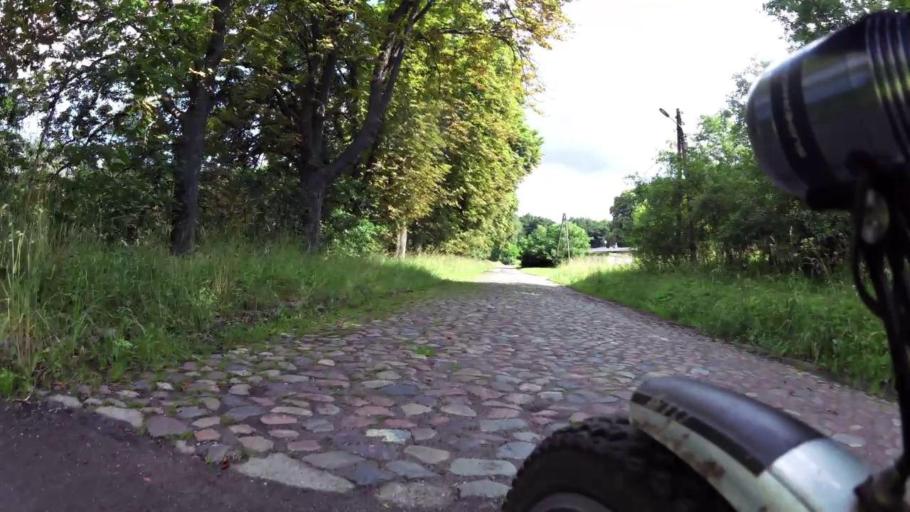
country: PL
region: West Pomeranian Voivodeship
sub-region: Powiat swidwinski
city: Rabino
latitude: 53.8112
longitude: 15.8913
